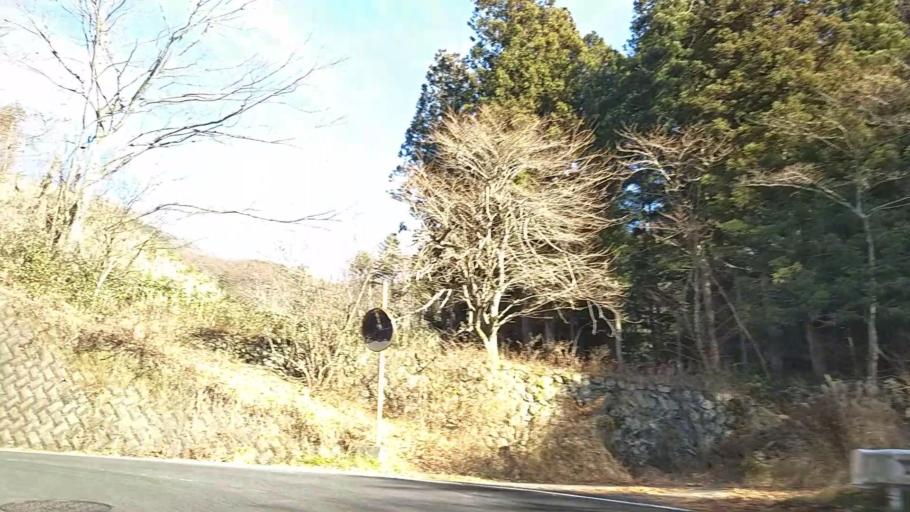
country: JP
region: Yamanashi
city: Otsuki
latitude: 35.5113
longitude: 138.9589
